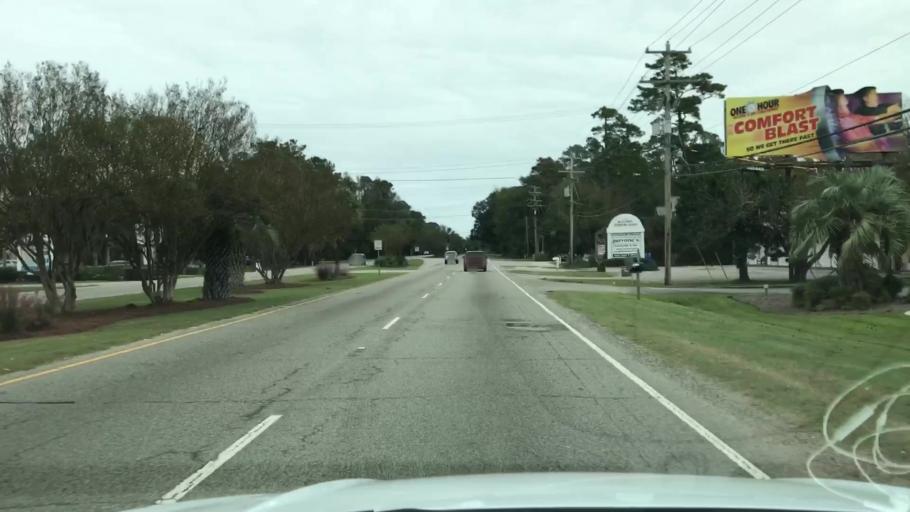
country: US
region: South Carolina
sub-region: Georgetown County
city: Murrells Inlet
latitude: 33.4737
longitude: -79.1036
